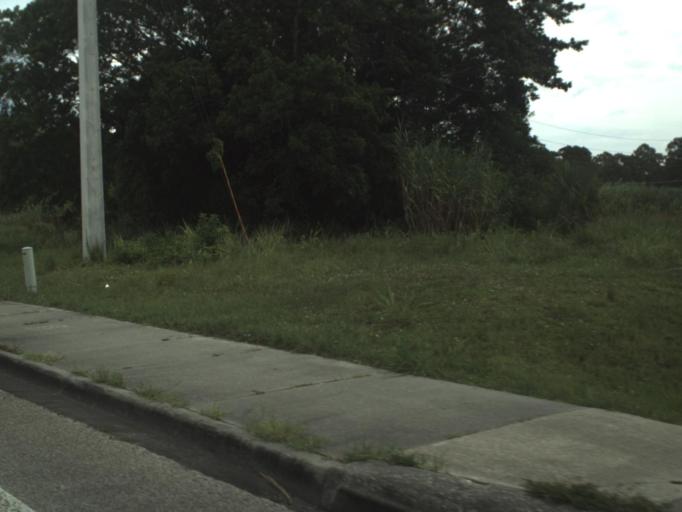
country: US
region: Florida
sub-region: Martin County
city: Palm City
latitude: 27.1622
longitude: -80.2483
